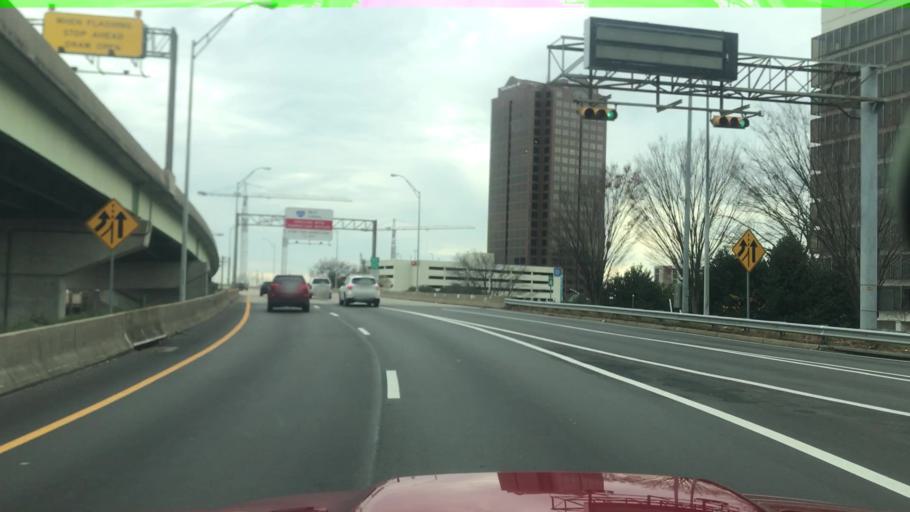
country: US
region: Virginia
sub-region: City of Norfolk
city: Norfolk
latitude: 36.8450
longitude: -76.2841
